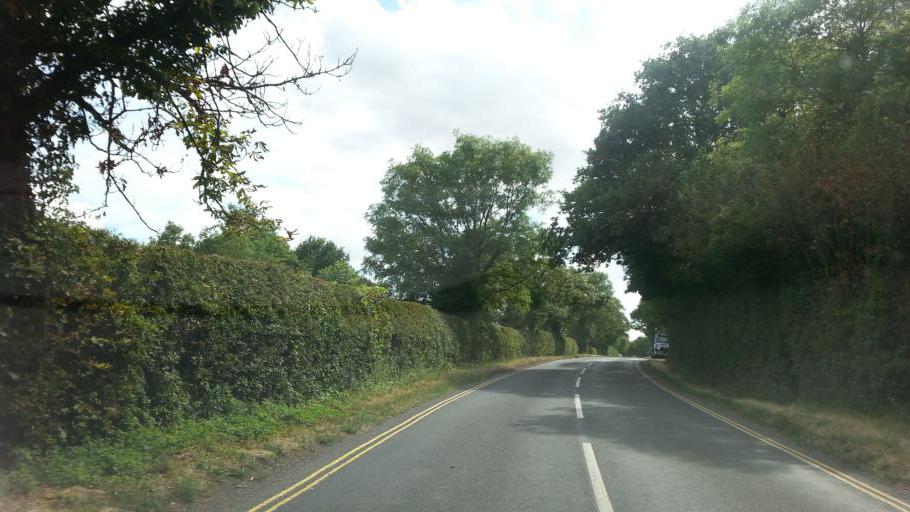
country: GB
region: England
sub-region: Northamptonshire
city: Silverstone
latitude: 52.0647
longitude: -1.0262
